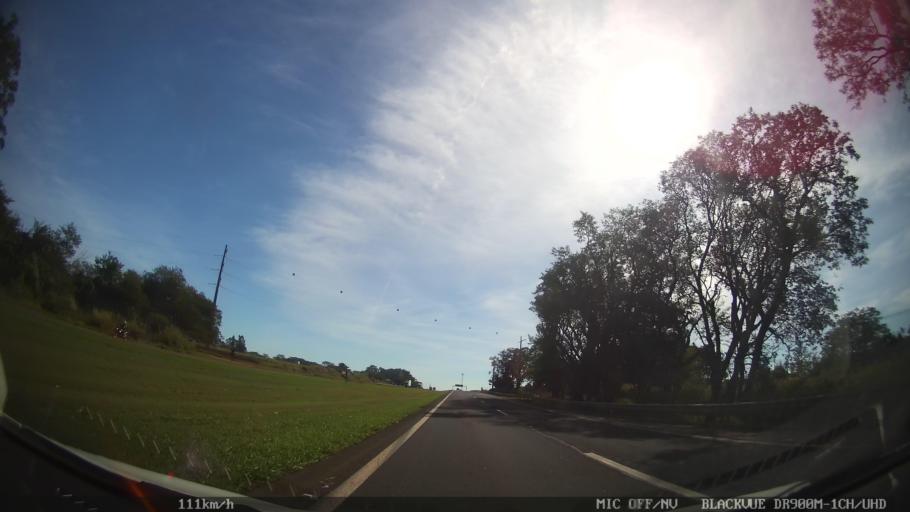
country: BR
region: Sao Paulo
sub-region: Leme
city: Leme
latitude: -22.2287
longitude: -47.3913
